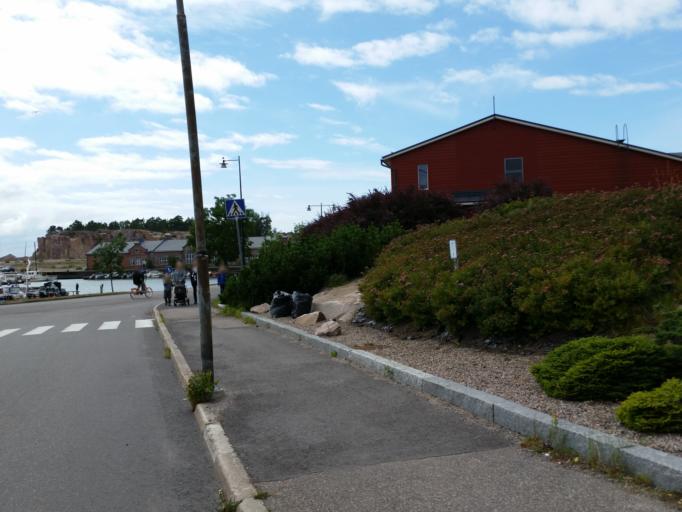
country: FI
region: Uusimaa
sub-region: Raaseporin
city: Hanko
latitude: 59.8219
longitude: 22.9649
